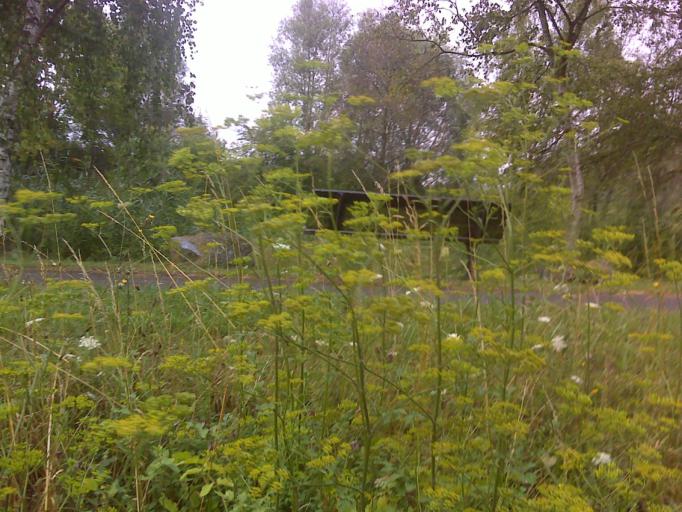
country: FR
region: Nord-Pas-de-Calais
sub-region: Departement du Nord
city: Conde-sur-l'Escaut
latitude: 50.4497
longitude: 3.6027
